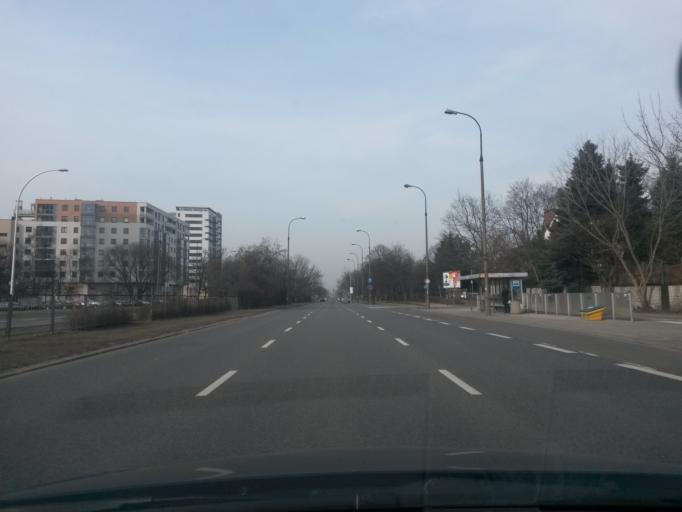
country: PL
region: Masovian Voivodeship
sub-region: Warszawa
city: Mokotow
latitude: 52.1792
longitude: 21.0588
